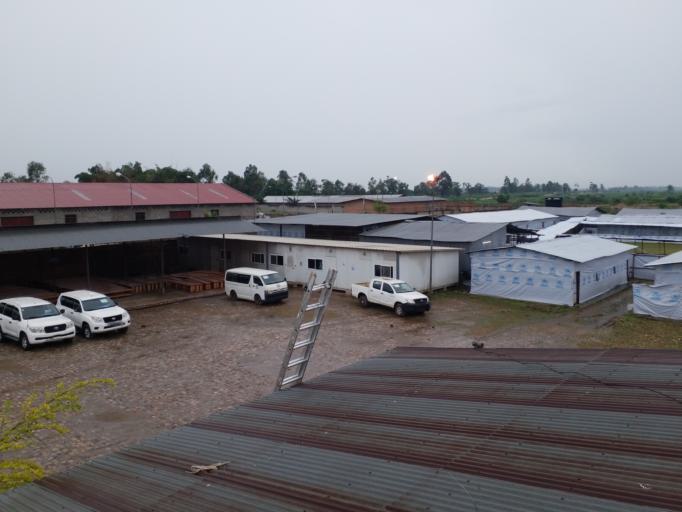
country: BI
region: Bujumbura Mairie
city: Bujumbura
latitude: -3.3540
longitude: 29.3300
